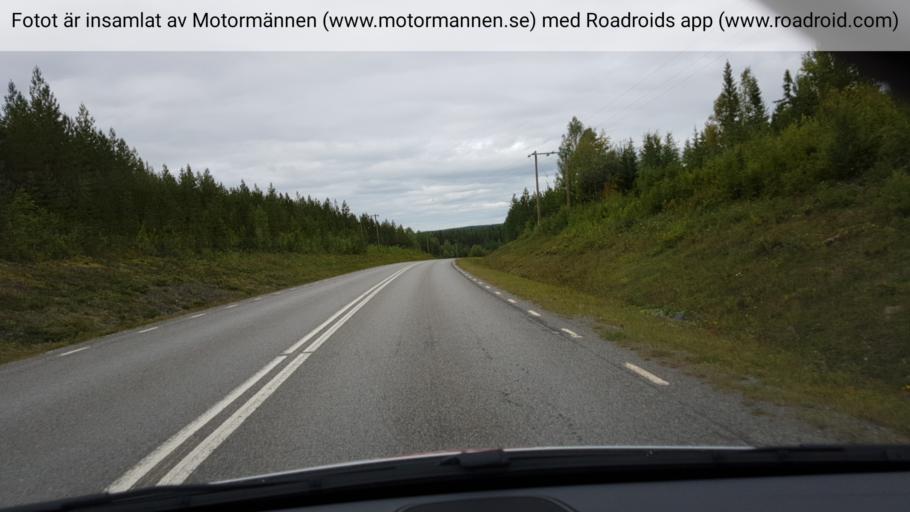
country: SE
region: Jaemtland
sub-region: Stroemsunds Kommun
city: Stroemsund
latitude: 64.2359
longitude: 15.4597
